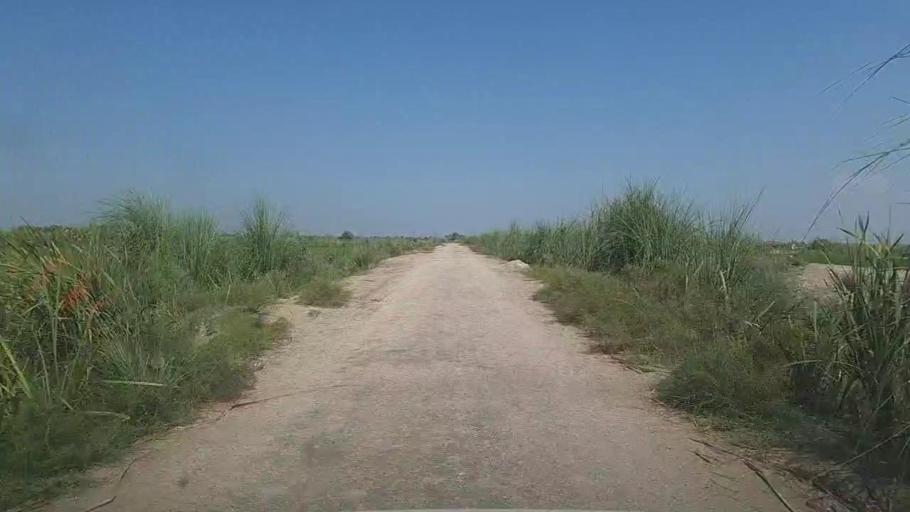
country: PK
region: Sindh
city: Kandhkot
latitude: 28.2977
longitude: 69.2072
